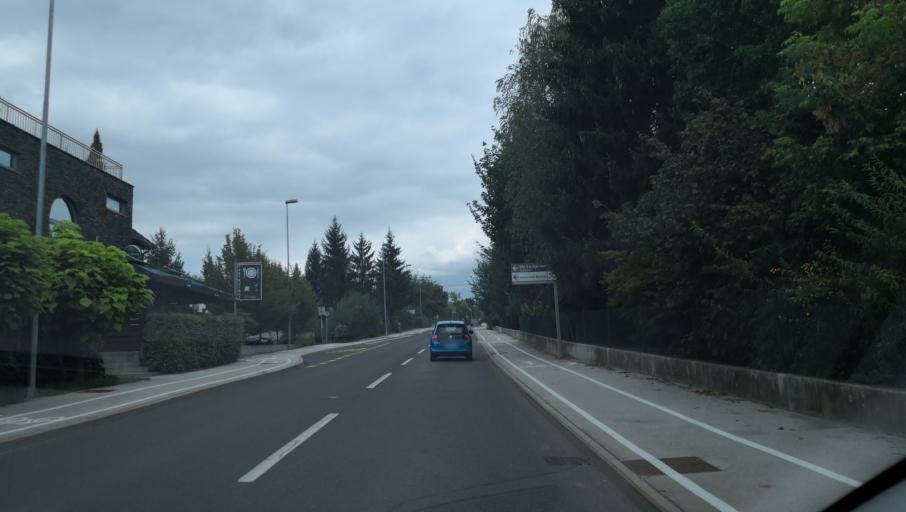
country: SI
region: Novo Mesto
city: Novo Mesto
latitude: 45.7899
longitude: 15.1789
